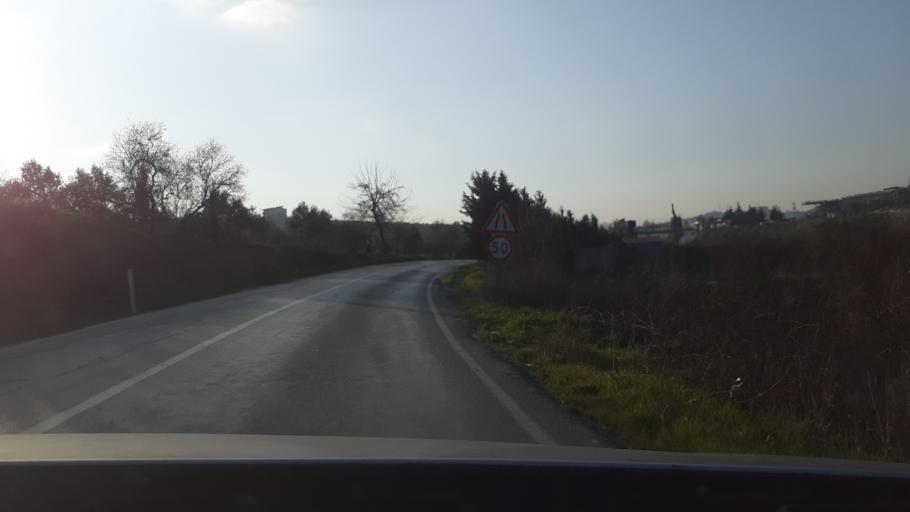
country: TR
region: Hatay
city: Fatikli
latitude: 36.1093
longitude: 36.2737
